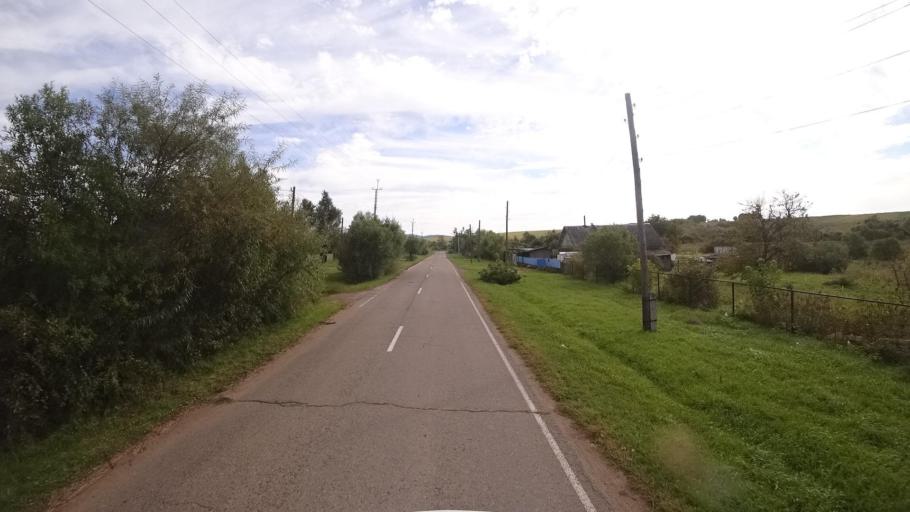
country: RU
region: Primorskiy
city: Dostoyevka
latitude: 44.3234
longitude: 133.4765
